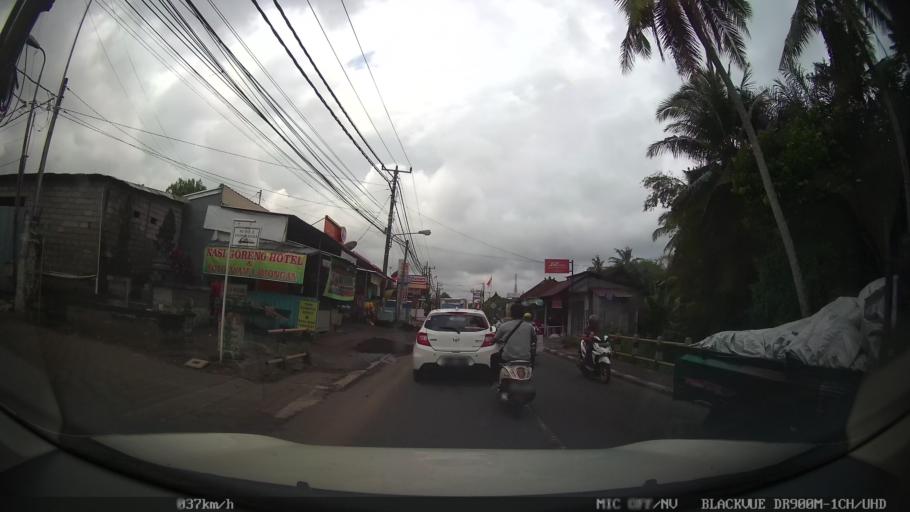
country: ID
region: Bali
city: Banjar Bucu
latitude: -8.5867
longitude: 115.2113
